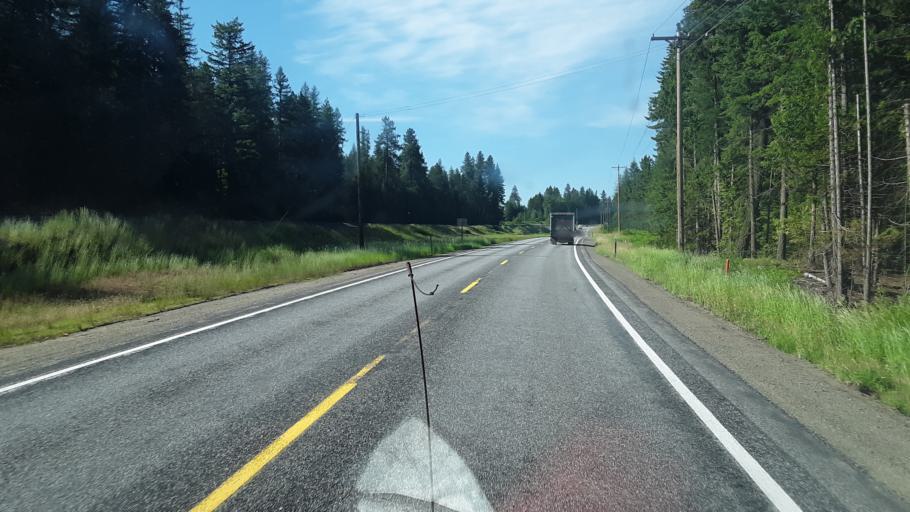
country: US
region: Idaho
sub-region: Bonner County
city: Ponderay
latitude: 48.5062
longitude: -116.4460
